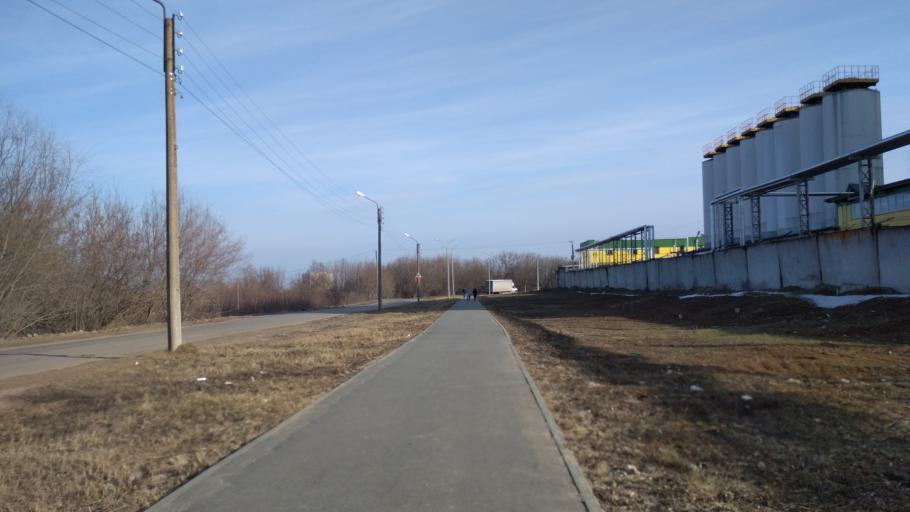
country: RU
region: Chuvashia
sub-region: Cheboksarskiy Rayon
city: Cheboksary
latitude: 56.1359
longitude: 47.3136
